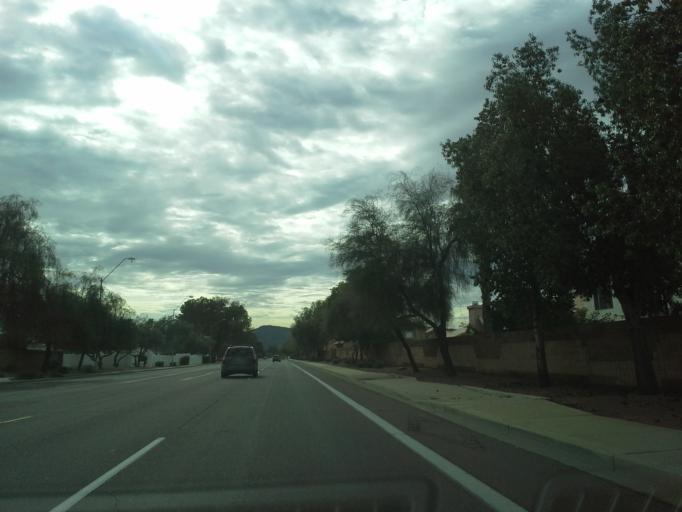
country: US
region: Arizona
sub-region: Maricopa County
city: Glendale
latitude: 33.6373
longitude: -112.0829
